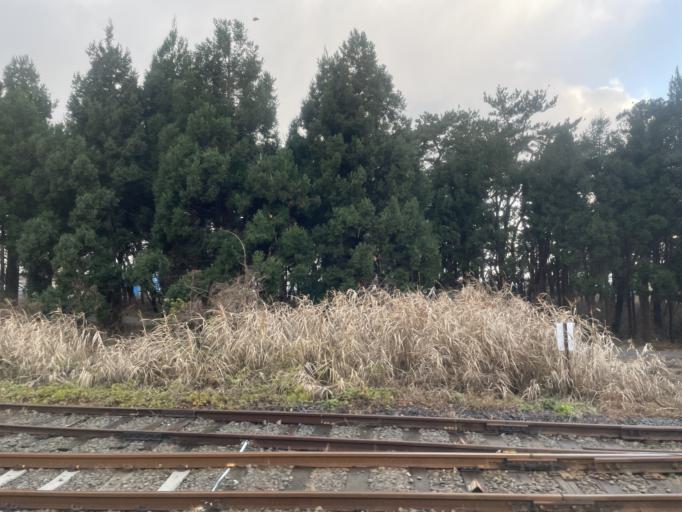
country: JP
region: Aomori
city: Mutsu
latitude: 41.0877
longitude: 141.2497
